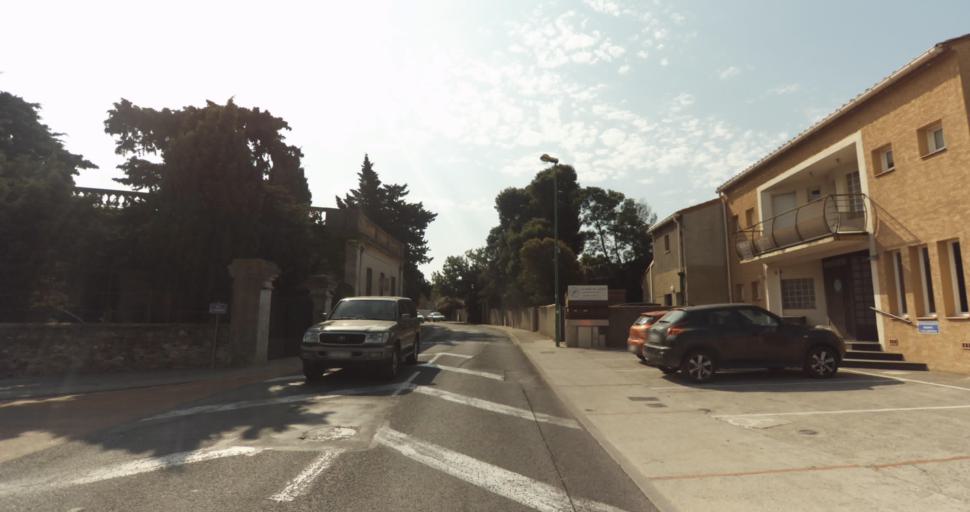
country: FR
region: Languedoc-Roussillon
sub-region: Departement des Pyrenees-Orientales
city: Latour-Bas-Elne
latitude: 42.6068
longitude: 2.9997
